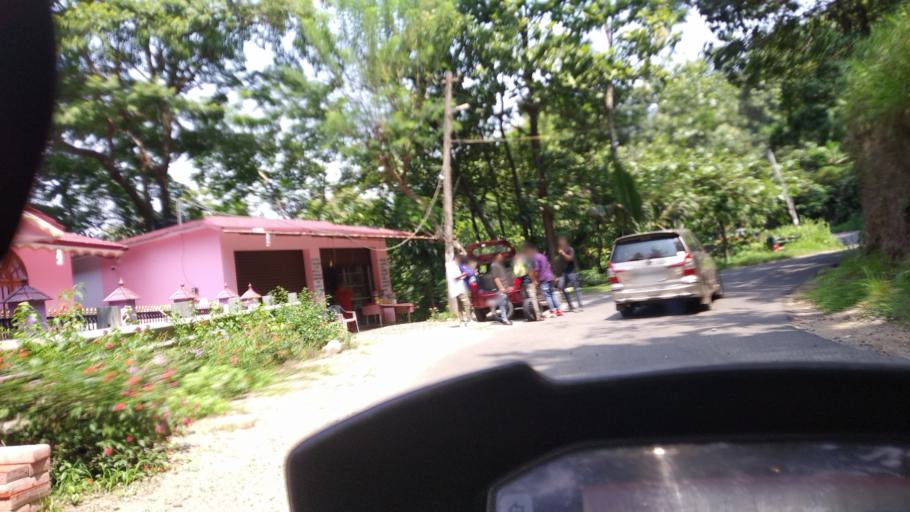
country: IN
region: Kerala
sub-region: Kottayam
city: Erattupetta
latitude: 9.6961
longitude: 76.8660
